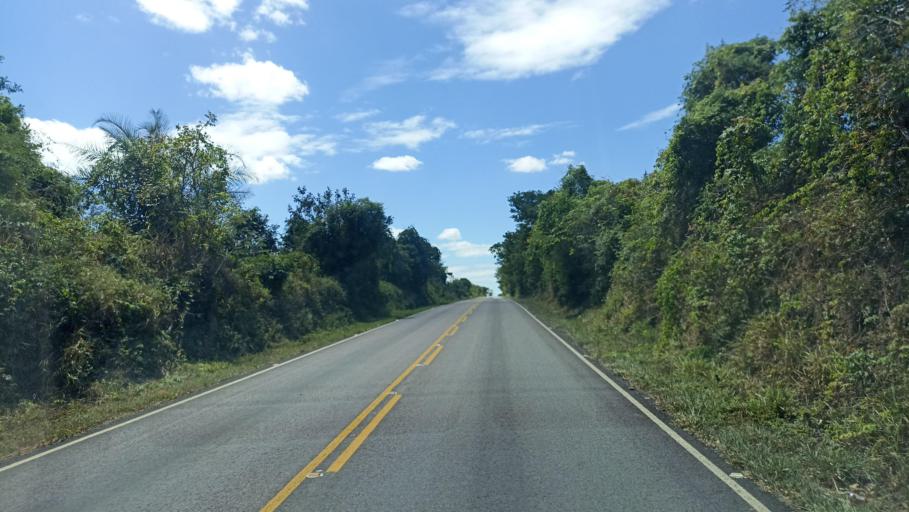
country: BR
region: Bahia
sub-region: Andarai
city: Vera Cruz
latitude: -12.7506
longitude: -41.3274
